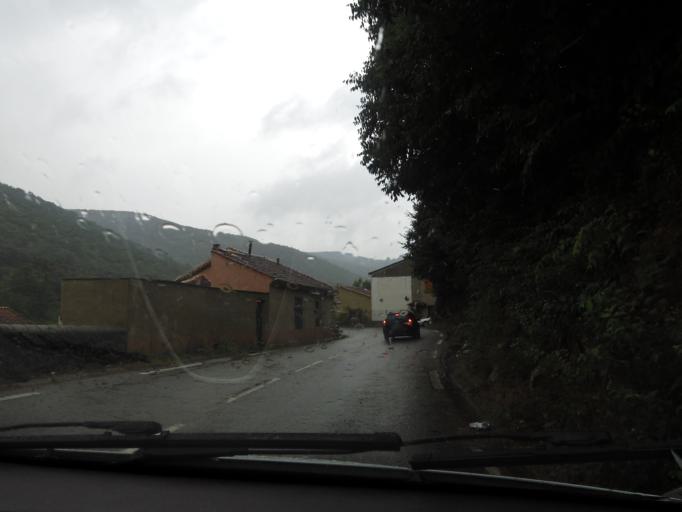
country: FR
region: Languedoc-Roussillon
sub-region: Departement du Gard
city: Les Salles-du-Gardon
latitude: 44.2038
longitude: 4.0333
